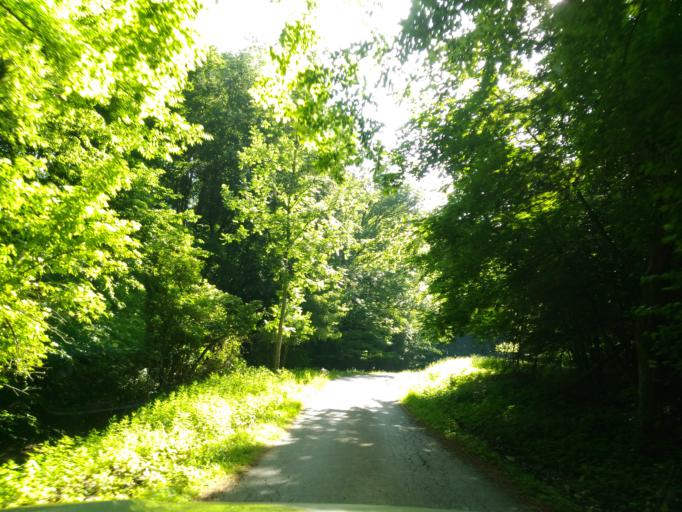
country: HU
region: Baranya
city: Hosszuheteny
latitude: 46.2179
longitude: 18.3554
